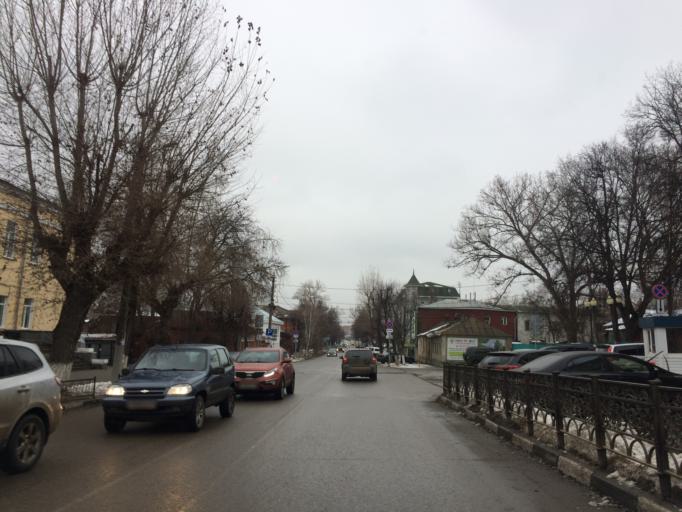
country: RU
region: Tula
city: Tula
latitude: 54.1872
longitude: 37.6116
